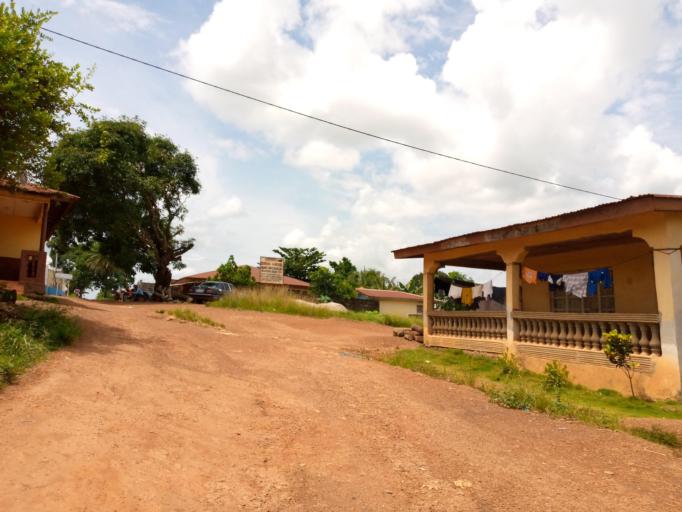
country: SL
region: Northern Province
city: Magburaka
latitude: 8.7256
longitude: -11.9370
